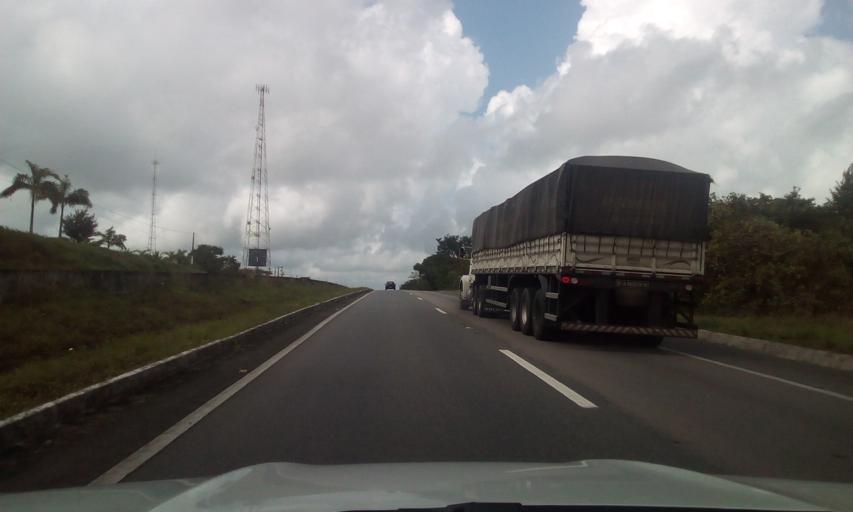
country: BR
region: Paraiba
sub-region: Conde
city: Conde
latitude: -7.3235
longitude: -34.9470
